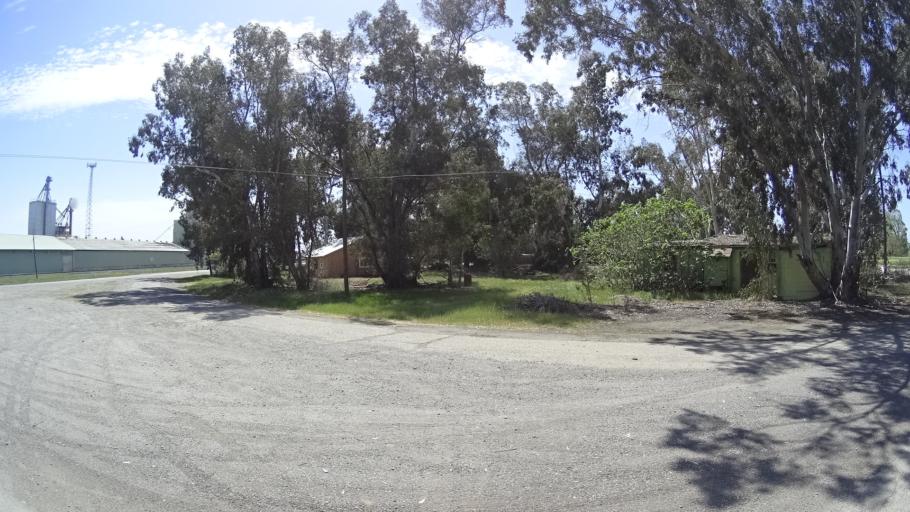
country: US
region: California
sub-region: Glenn County
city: Willows
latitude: 39.6245
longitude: -122.1938
